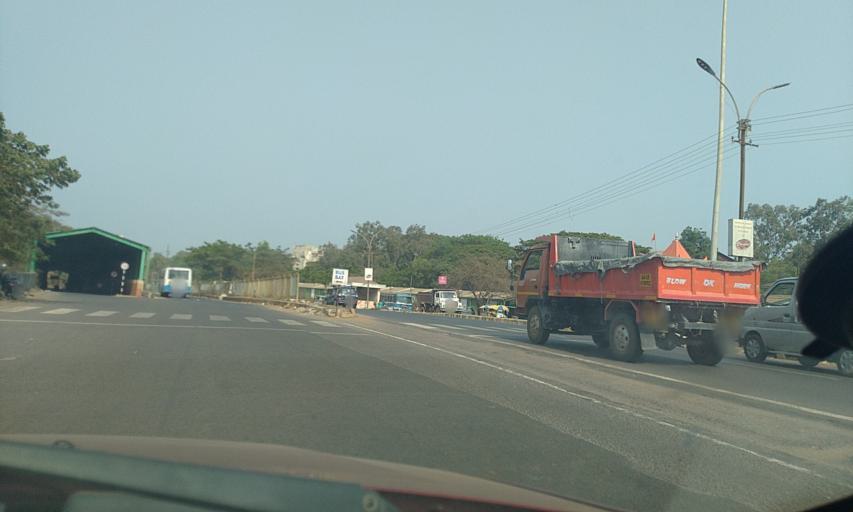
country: IN
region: Goa
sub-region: North Goa
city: Bambolim
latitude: 15.4649
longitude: 73.8569
